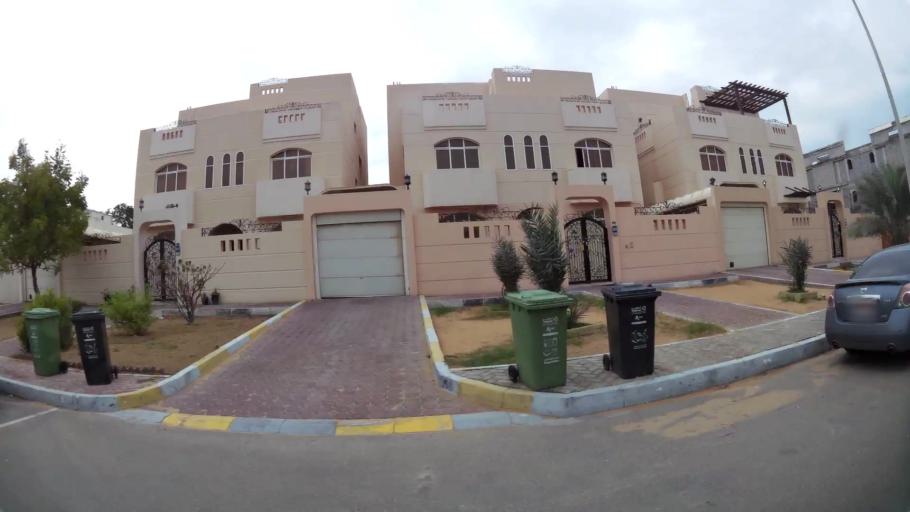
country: AE
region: Abu Dhabi
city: Abu Dhabi
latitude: 24.4346
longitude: 54.4016
